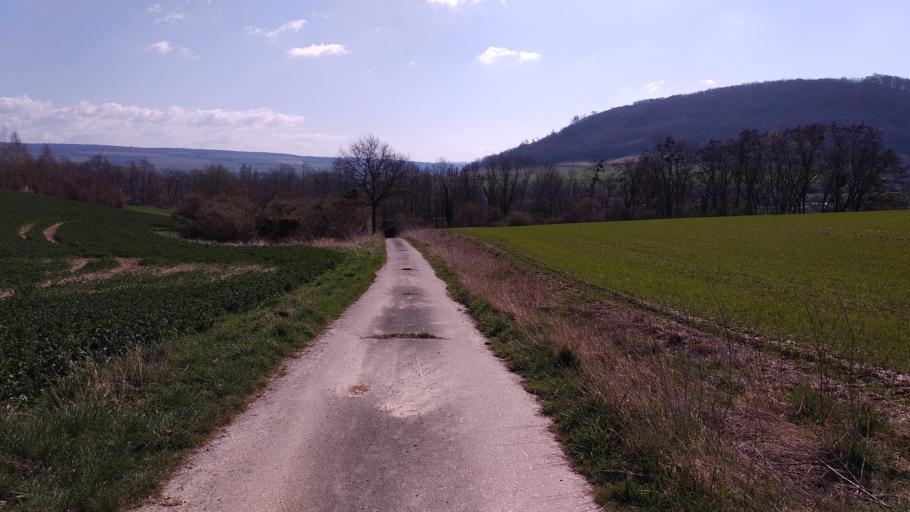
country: DE
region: North Rhine-Westphalia
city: Beverungen
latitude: 51.6592
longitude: 9.3453
